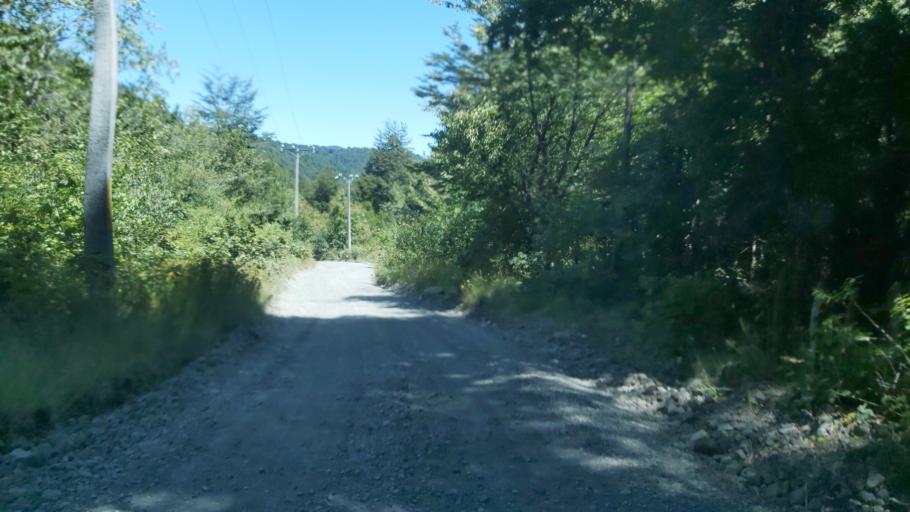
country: CL
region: Araucania
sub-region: Provincia de Cautin
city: Vilcun
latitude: -38.4723
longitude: -71.6725
